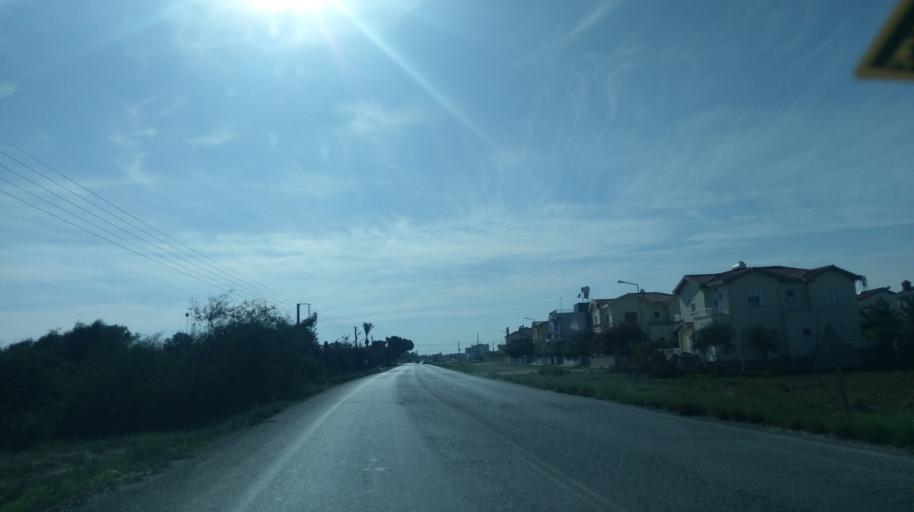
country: CY
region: Ammochostos
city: Trikomo
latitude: 35.3035
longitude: 33.9405
